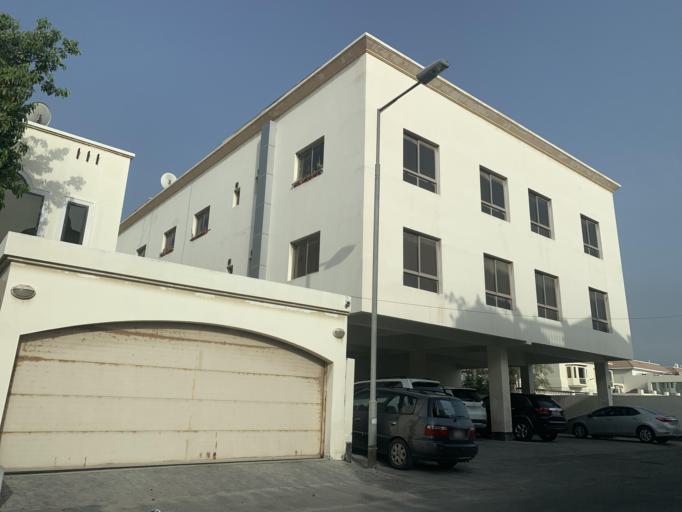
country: BH
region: Northern
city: Madinat `Isa
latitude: 26.1928
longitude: 50.5648
